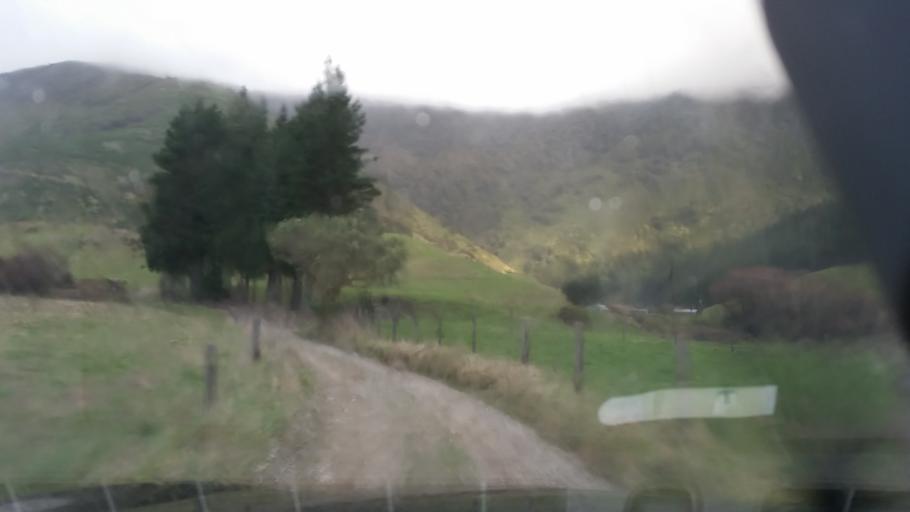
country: NZ
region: Marlborough
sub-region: Marlborough District
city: Picton
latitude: -41.2151
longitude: 173.6968
